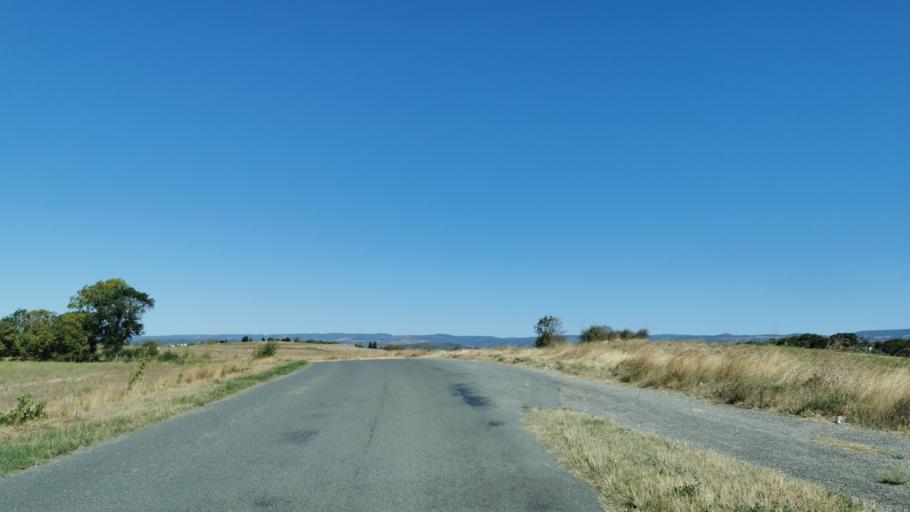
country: FR
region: Languedoc-Roussillon
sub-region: Departement de l'Aude
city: Conques-sur-Orbiel
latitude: 43.2543
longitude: 2.4257
